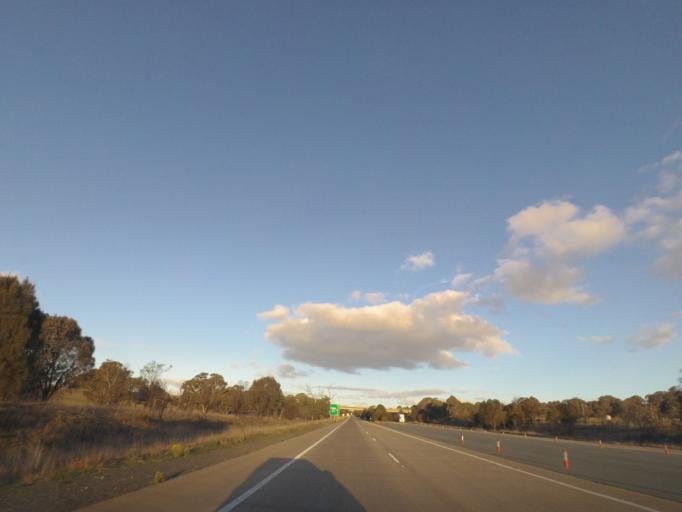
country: AU
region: New South Wales
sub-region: Yass Valley
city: Yass
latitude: -34.8069
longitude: 148.9282
